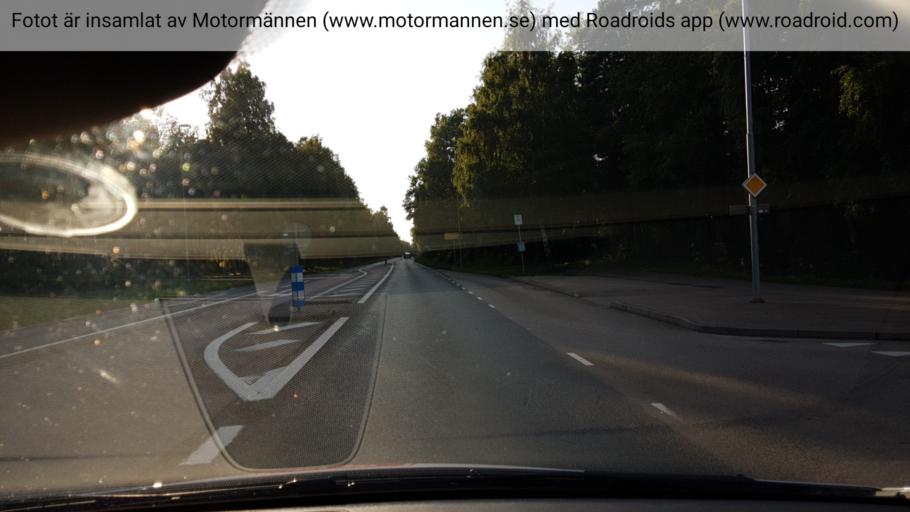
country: SE
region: Halland
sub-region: Halmstads Kommun
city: Mjallby
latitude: 56.6550
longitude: 12.7747
